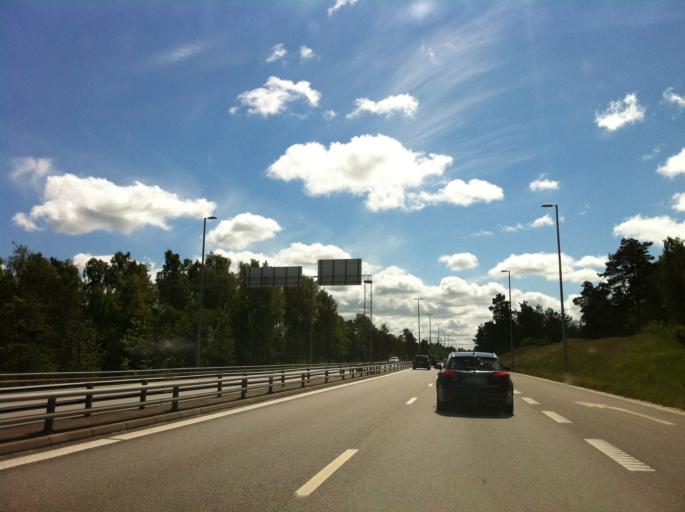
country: SE
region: Vaestra Goetaland
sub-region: Trollhattan
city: Trollhattan
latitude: 58.2753
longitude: 12.2997
